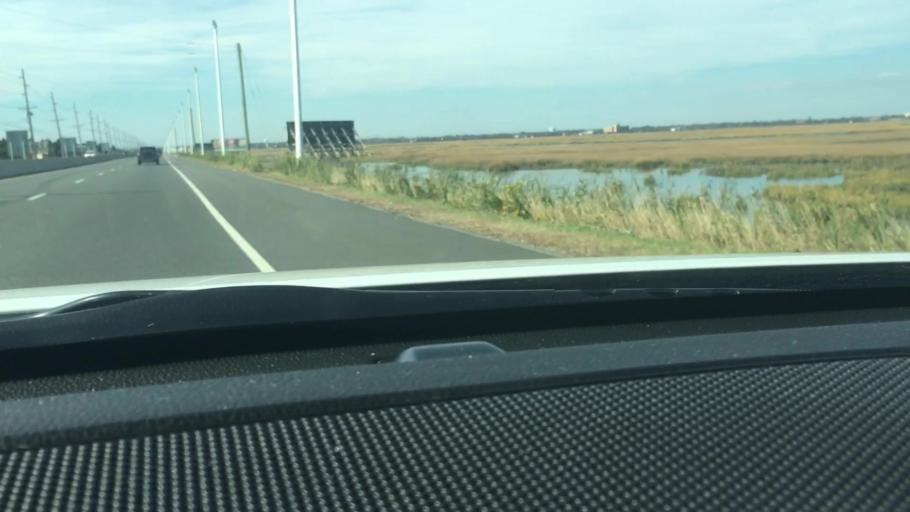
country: US
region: New Jersey
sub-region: Atlantic County
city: Ventnor City
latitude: 39.3867
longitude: -74.4674
